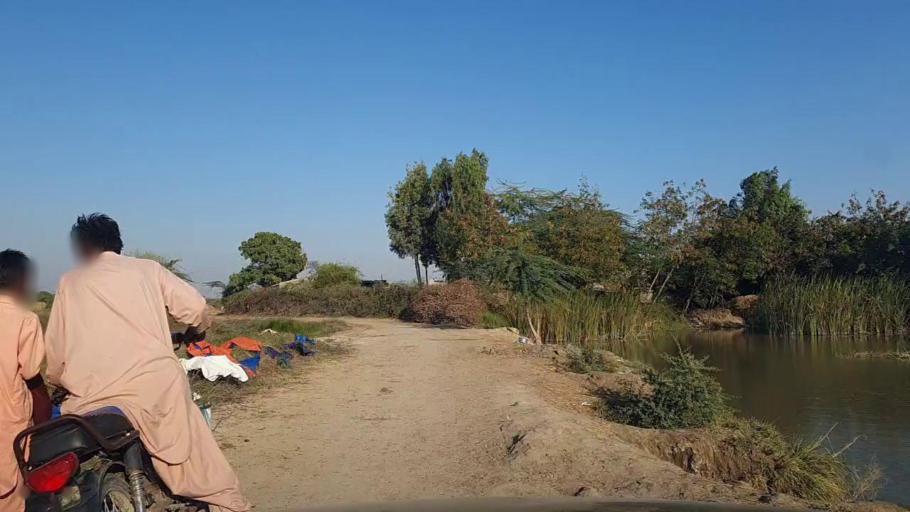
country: PK
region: Sindh
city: Mirpur Batoro
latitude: 24.6846
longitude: 68.3649
